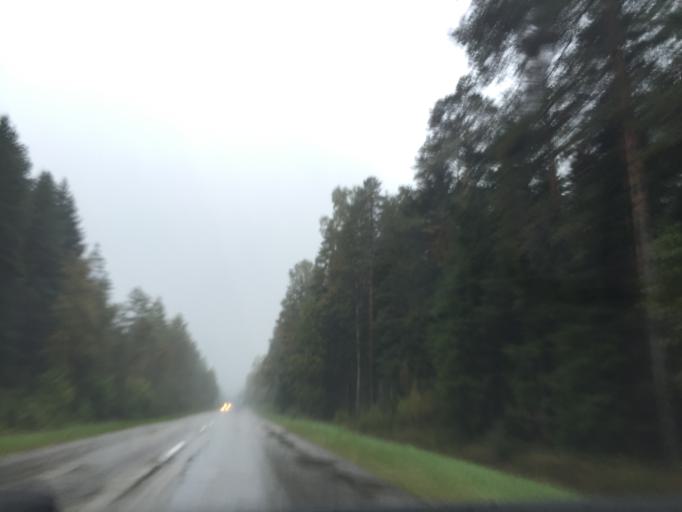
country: LV
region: Ropazu
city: Ropazi
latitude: 56.9922
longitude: 24.6418
